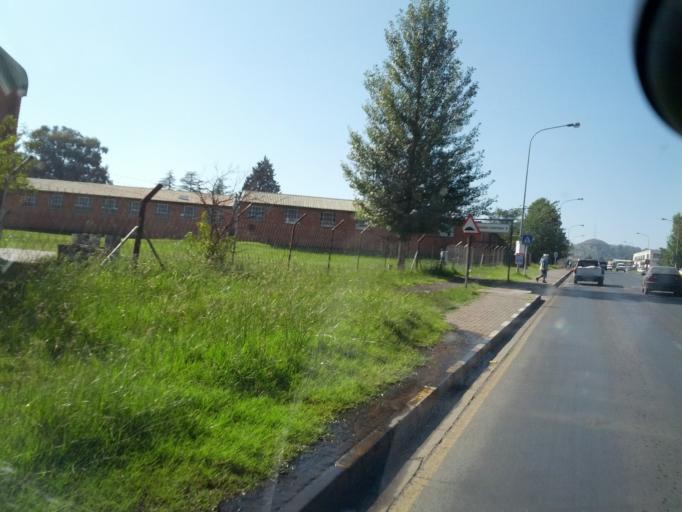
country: LS
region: Maseru
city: Maseru
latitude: -29.3031
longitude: 27.4827
